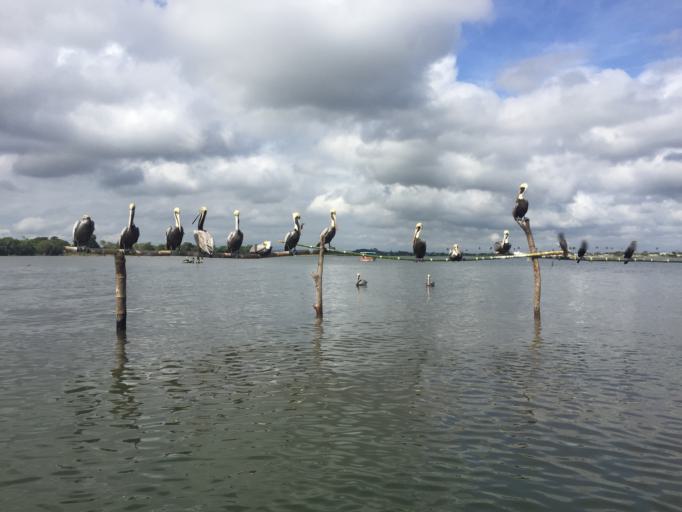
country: MX
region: Veracruz
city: Tecolutla
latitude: 20.4696
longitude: -97.0075
